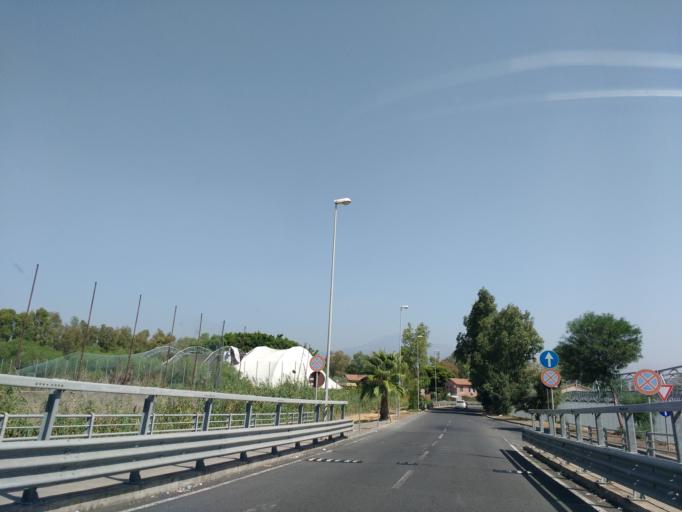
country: IT
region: Sicily
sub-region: Catania
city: Catania
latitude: 37.4716
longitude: 15.0674
